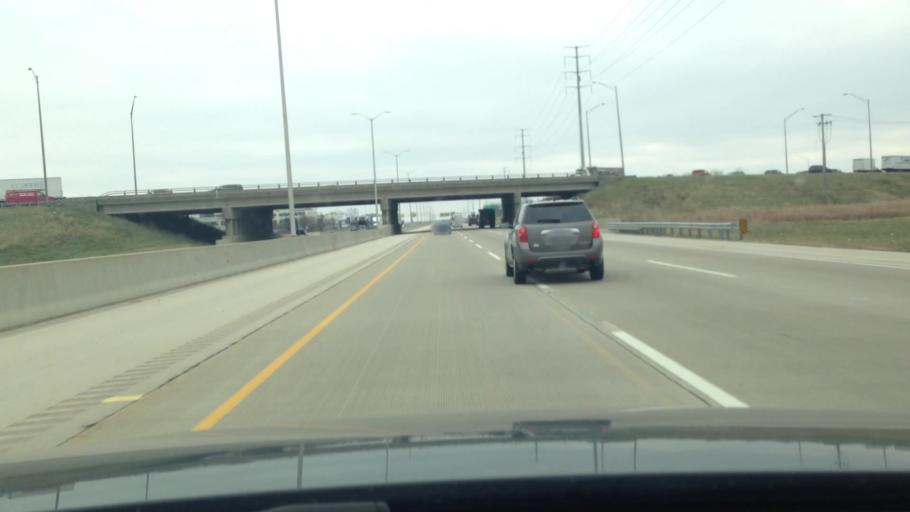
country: US
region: Illinois
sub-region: Kane County
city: Sleepy Hollow
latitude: 42.0813
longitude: -88.3370
